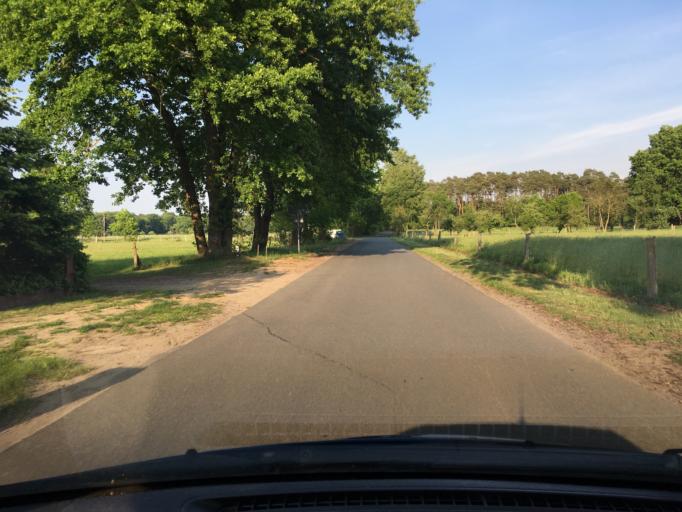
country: DE
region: Lower Saxony
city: Rullstorf
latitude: 53.2898
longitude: 10.5622
